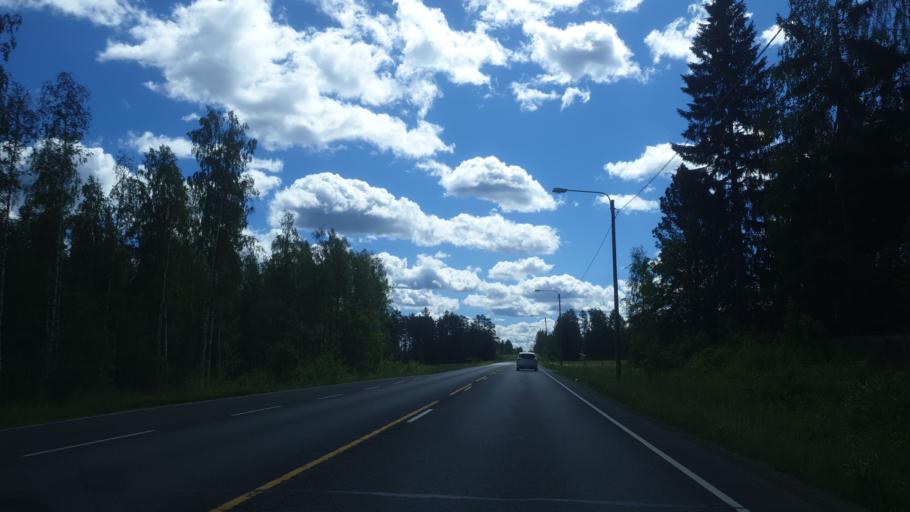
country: FI
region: Northern Savo
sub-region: Varkaus
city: Leppaevirta
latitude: 62.6355
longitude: 27.6122
